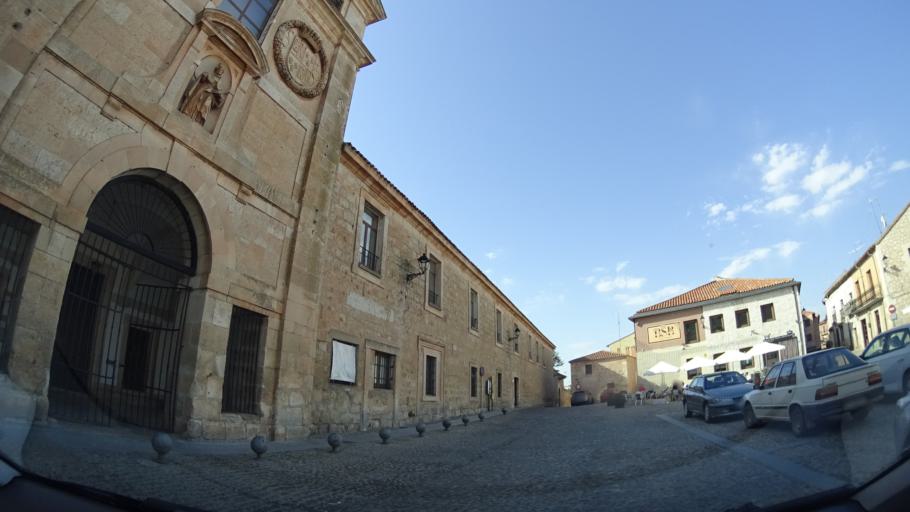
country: ES
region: Castille and Leon
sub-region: Provincia de Burgos
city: Lerma
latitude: 42.0256
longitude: -3.7553
